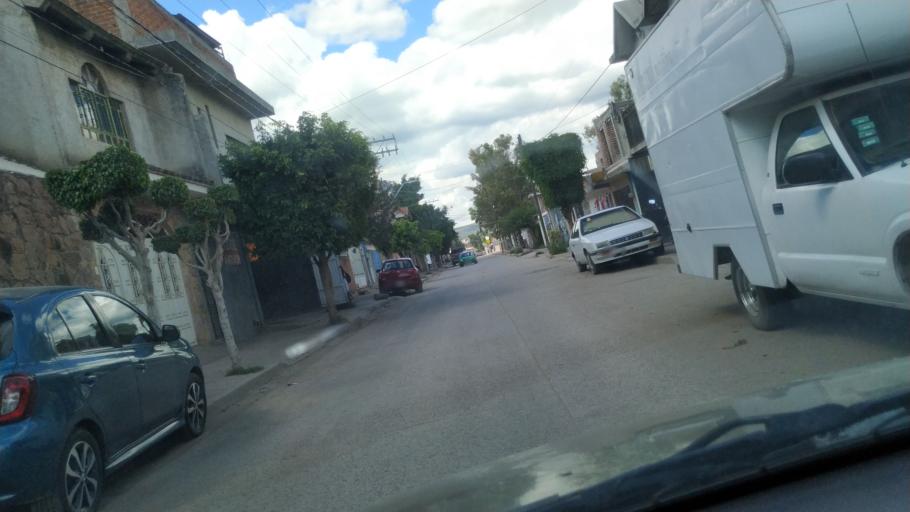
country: MX
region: Guanajuato
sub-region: Leon
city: Medina
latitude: 21.1455
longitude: -101.6289
